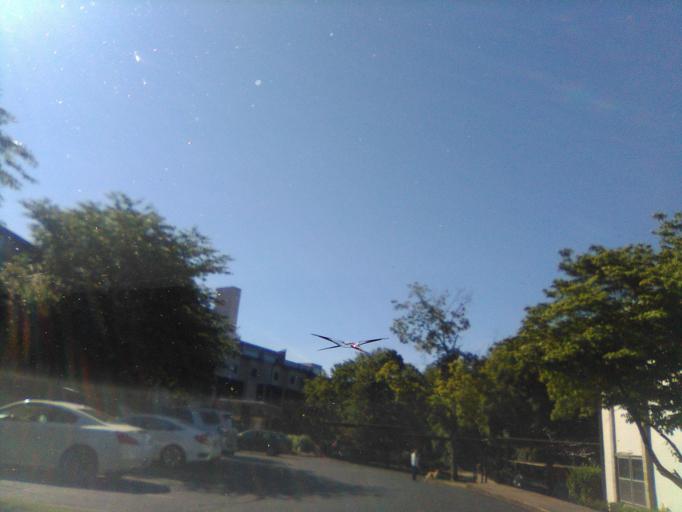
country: US
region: Tennessee
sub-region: Davidson County
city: Belle Meade
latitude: 36.1223
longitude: -86.8481
